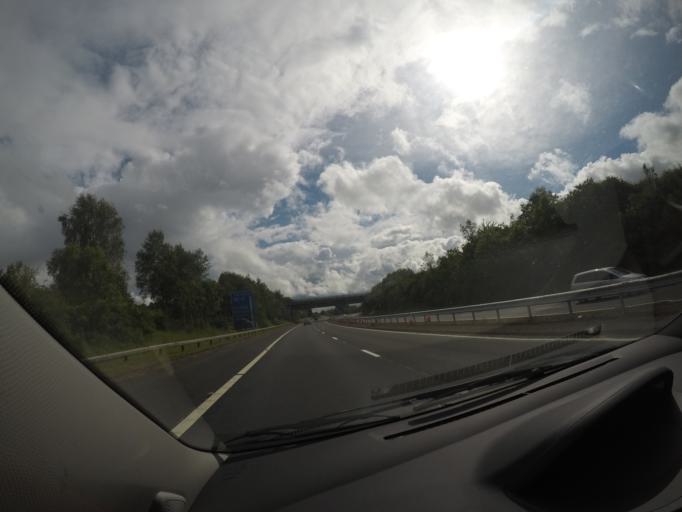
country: GB
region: Scotland
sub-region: North Lanarkshire
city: Glenboig
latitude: 55.8946
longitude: -4.0693
